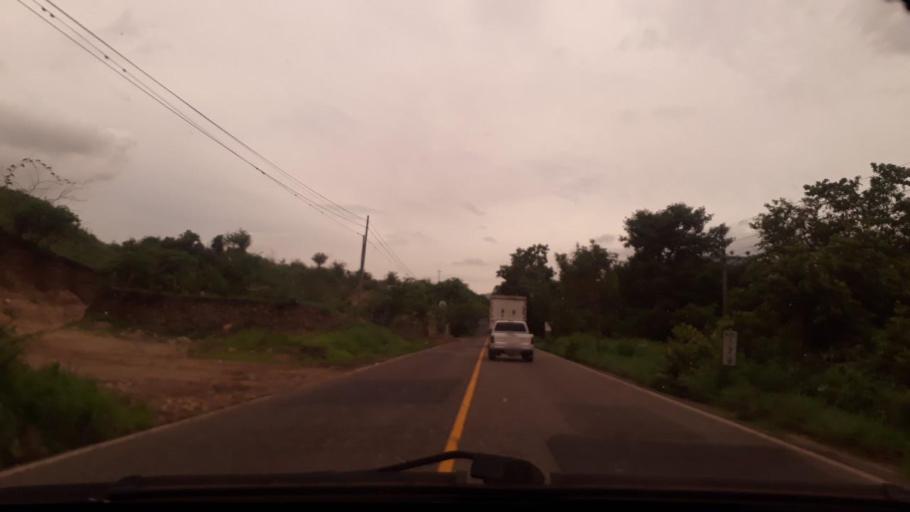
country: GT
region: Chiquimula
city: San Jose La Arada
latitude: 14.7366
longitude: -89.5630
